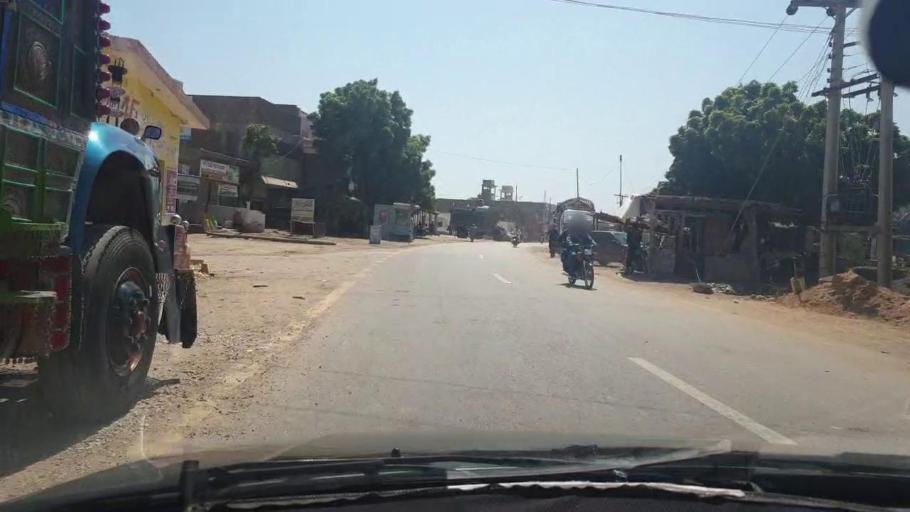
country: PK
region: Sindh
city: Chambar
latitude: 25.2998
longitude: 68.8107
